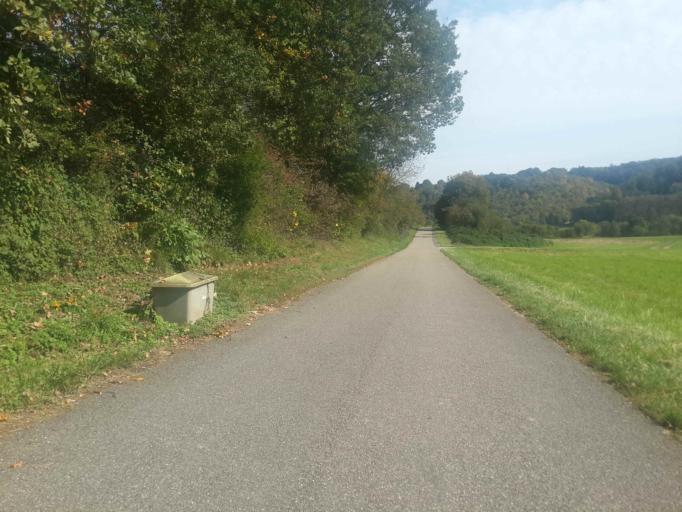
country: DE
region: Baden-Wuerttemberg
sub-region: Regierungsbezirk Stuttgart
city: Mockmuhl
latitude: 49.3042
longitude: 9.3537
